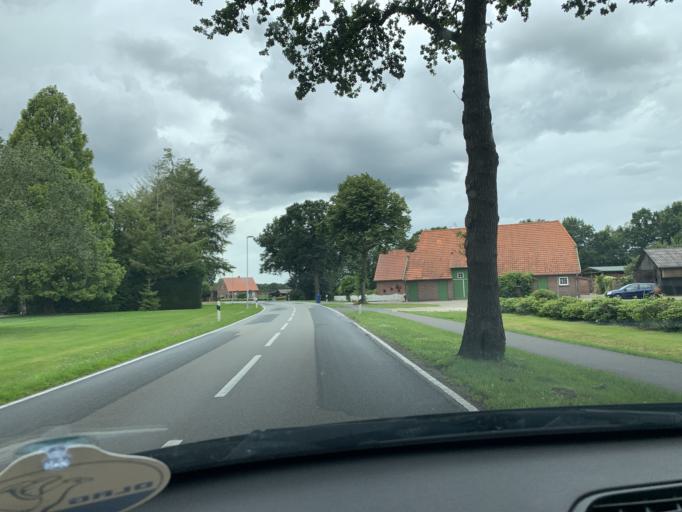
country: DE
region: Lower Saxony
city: Edewecht
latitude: 53.1294
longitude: 7.8954
